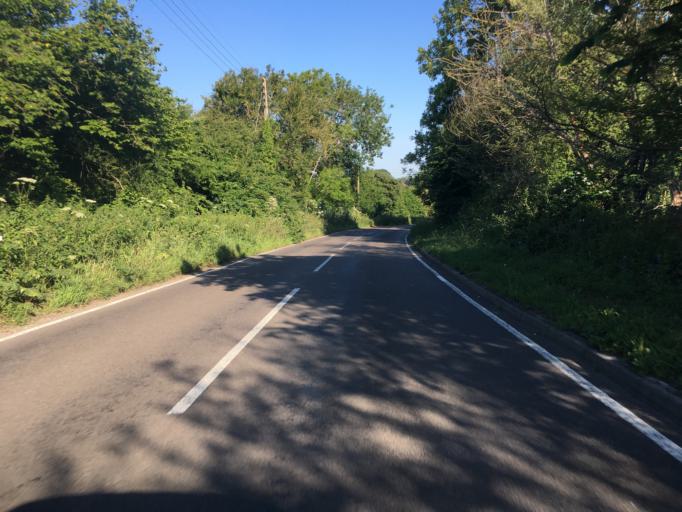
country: GB
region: England
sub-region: South Gloucestershire
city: Siston
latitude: 51.4652
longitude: -2.4668
